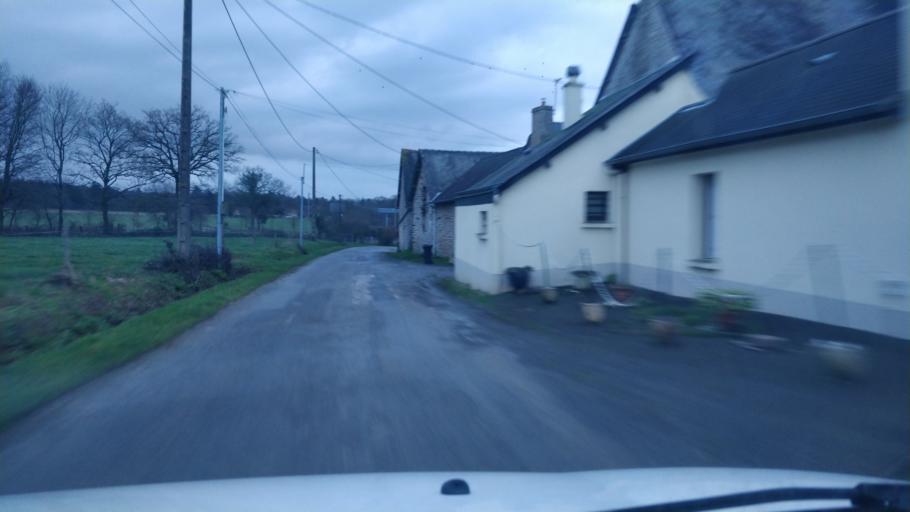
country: FR
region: Brittany
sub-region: Departement d'Ille-et-Vilaine
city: Livre-sur-Changeon
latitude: 48.1885
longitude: -1.3099
